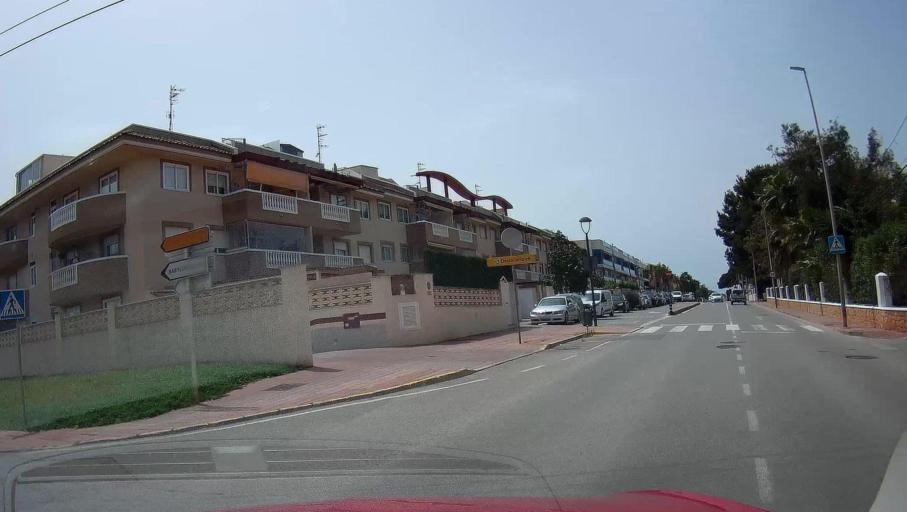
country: ES
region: Balearic Islands
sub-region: Illes Balears
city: Santa Eularia des Riu
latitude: 38.9916
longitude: 1.5466
